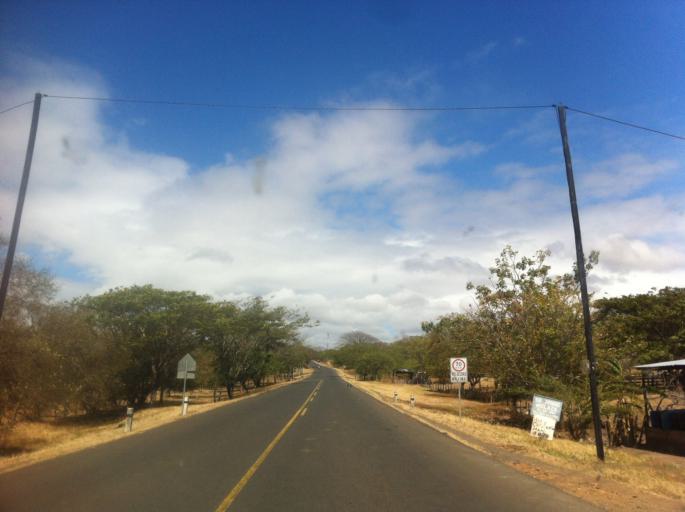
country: NI
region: Chontales
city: Acoyapa
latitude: 12.0121
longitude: -85.2433
